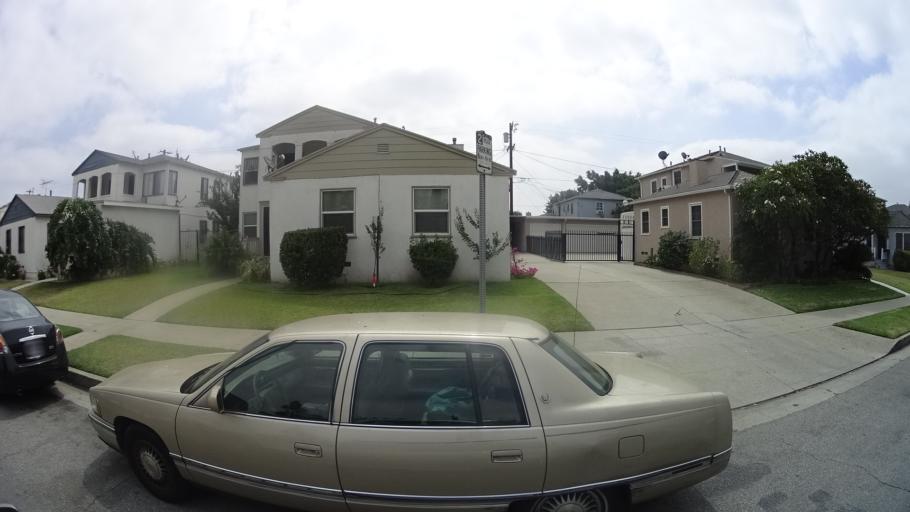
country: US
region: California
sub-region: Los Angeles County
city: View Park-Windsor Hills
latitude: 34.0221
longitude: -118.3461
